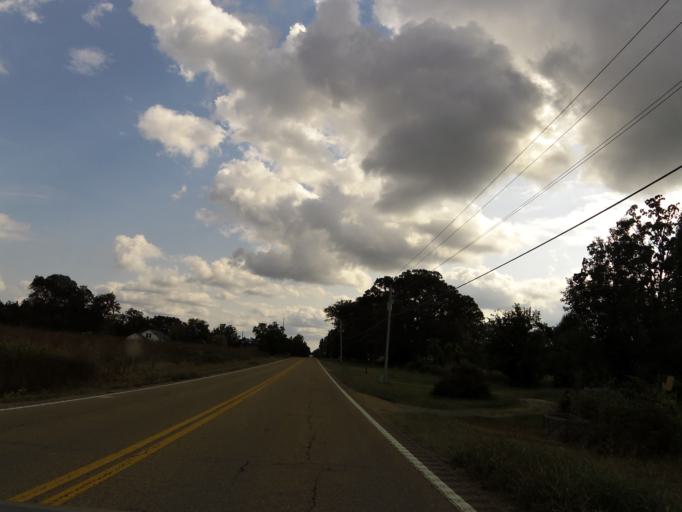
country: US
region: Mississippi
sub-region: Alcorn County
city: Farmington
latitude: 35.0217
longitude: -88.4549
